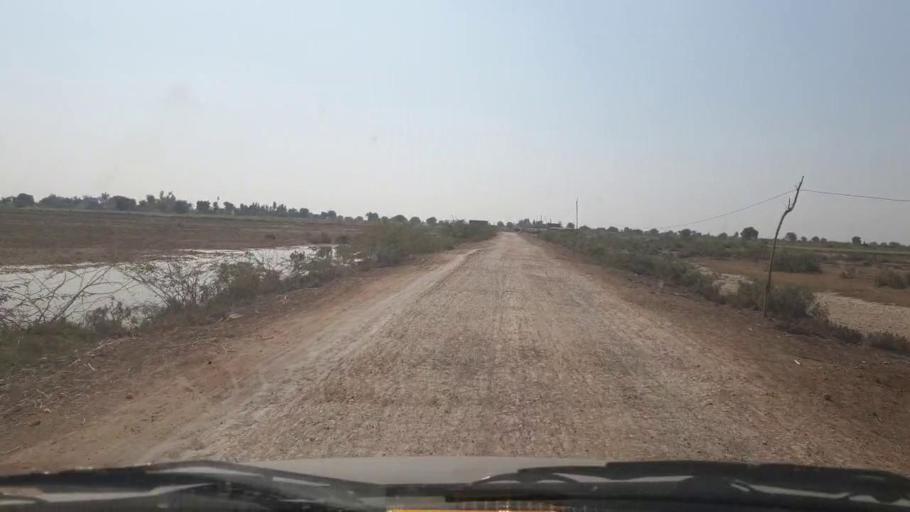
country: PK
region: Sindh
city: Samaro
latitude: 25.2245
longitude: 69.3333
